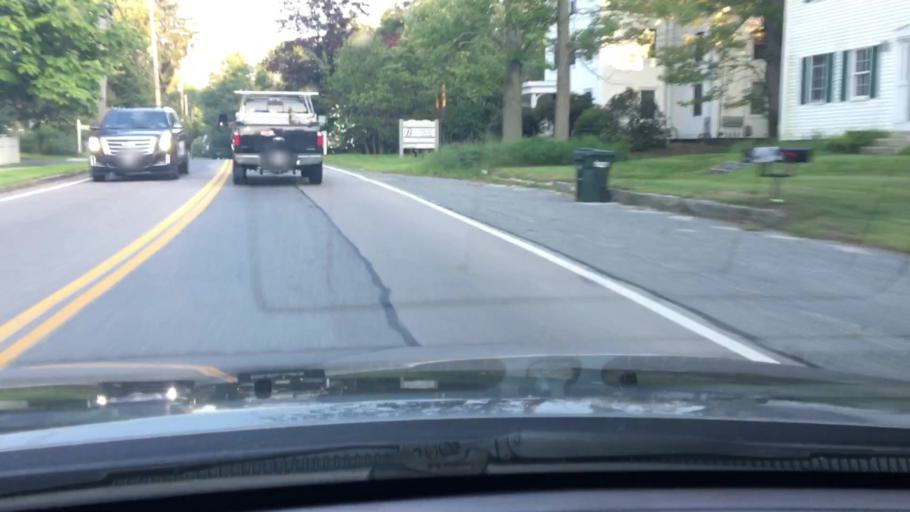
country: US
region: Massachusetts
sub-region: Middlesex County
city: Hopkinton
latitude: 42.2377
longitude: -71.5622
